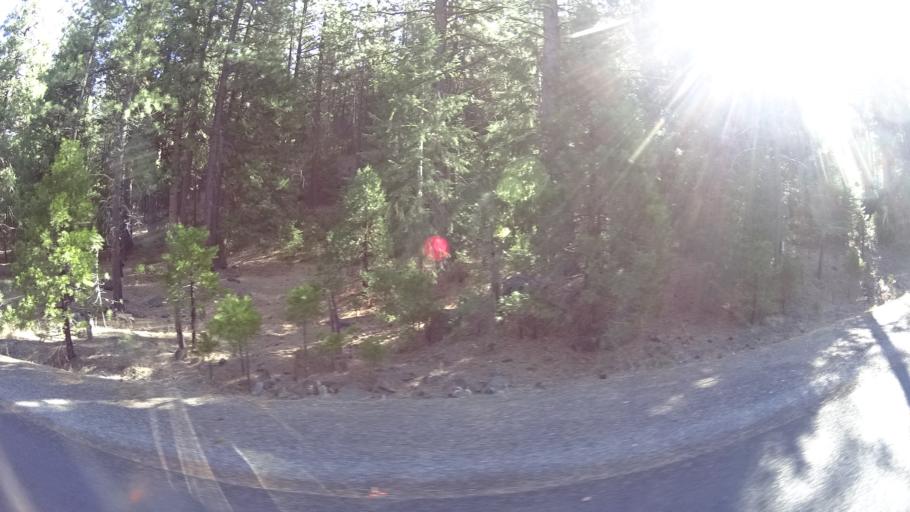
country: US
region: California
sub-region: Siskiyou County
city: Weed
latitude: 41.4218
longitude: -122.5019
